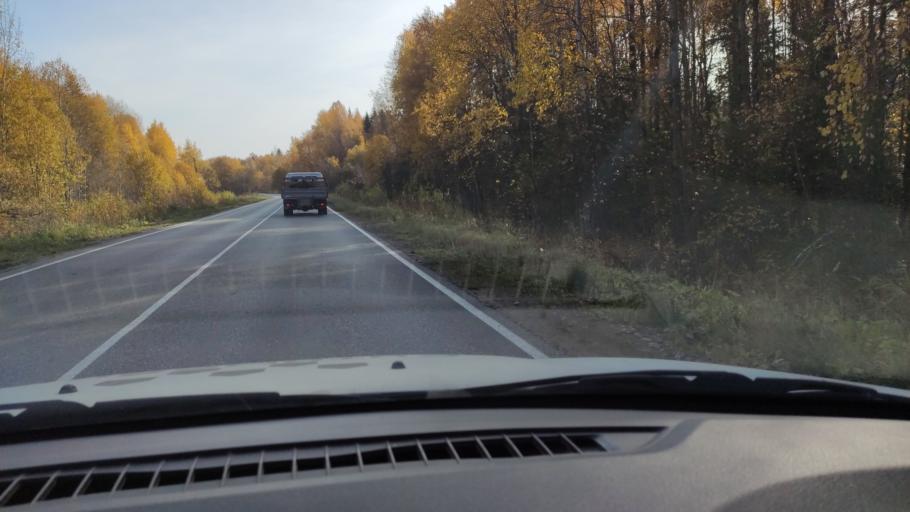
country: RU
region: Perm
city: Novyye Lyady
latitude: 58.0219
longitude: 56.6446
